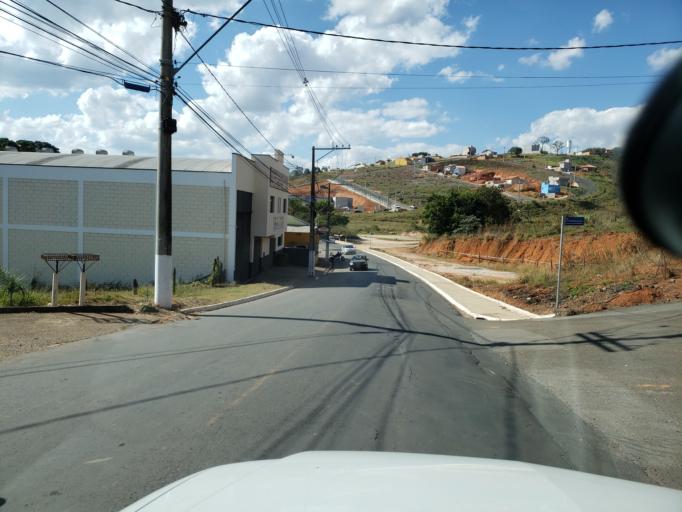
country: BR
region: Minas Gerais
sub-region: Monte Siao
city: Monte Siao
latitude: -22.4245
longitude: -46.5689
